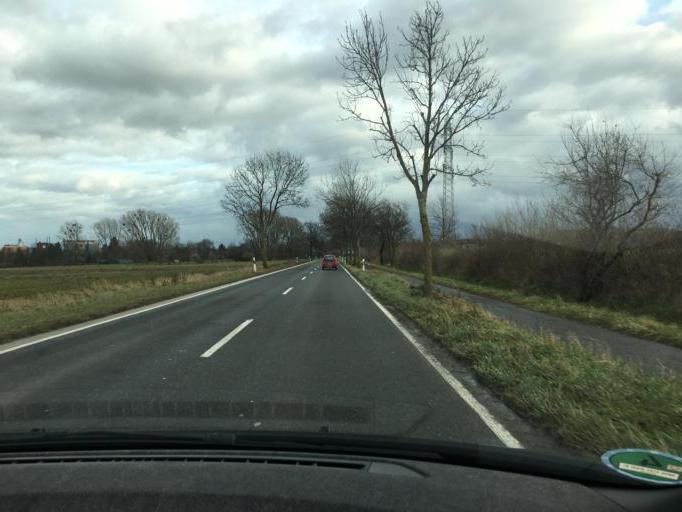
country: DE
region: North Rhine-Westphalia
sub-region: Regierungsbezirk Koln
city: Euskirchen
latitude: 50.6356
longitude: 6.8019
